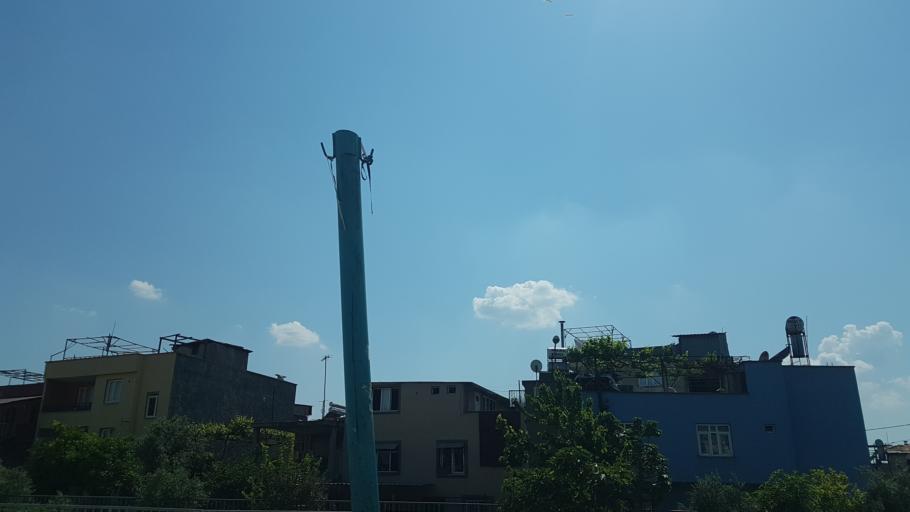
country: TR
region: Adana
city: Yuregir
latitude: 37.0148
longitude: 35.3853
